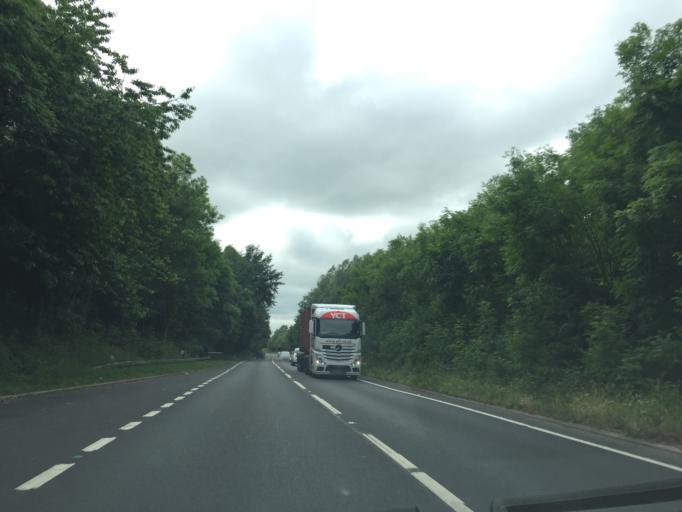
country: GB
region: England
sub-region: Dorset
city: Wimborne Minster
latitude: 50.7903
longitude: -1.9892
